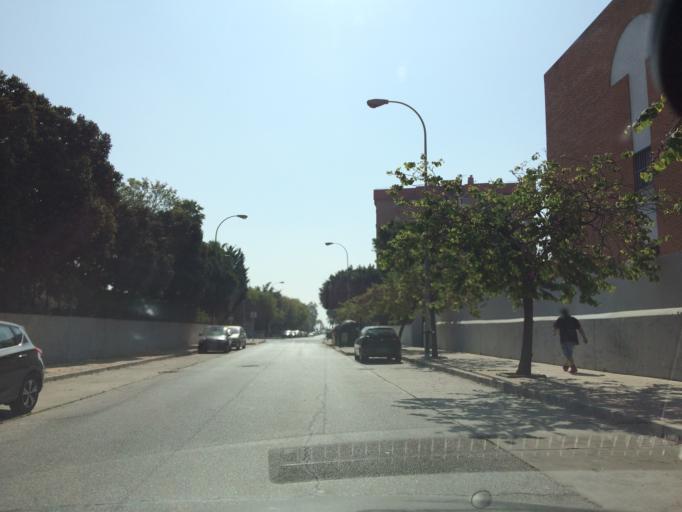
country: ES
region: Andalusia
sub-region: Provincia de Malaga
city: Malaga
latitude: 36.6925
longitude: -4.4465
